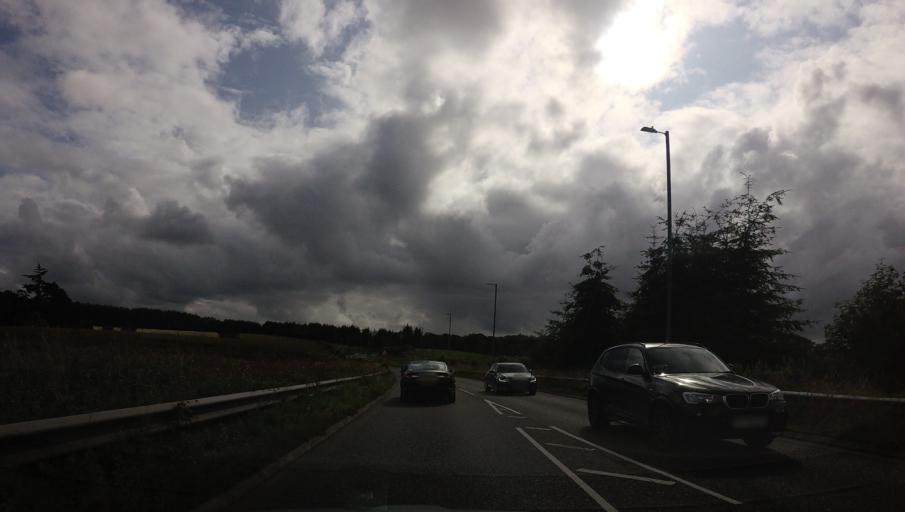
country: GB
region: Scotland
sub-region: Aberdeen City
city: Cults
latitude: 57.1480
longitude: -2.2003
